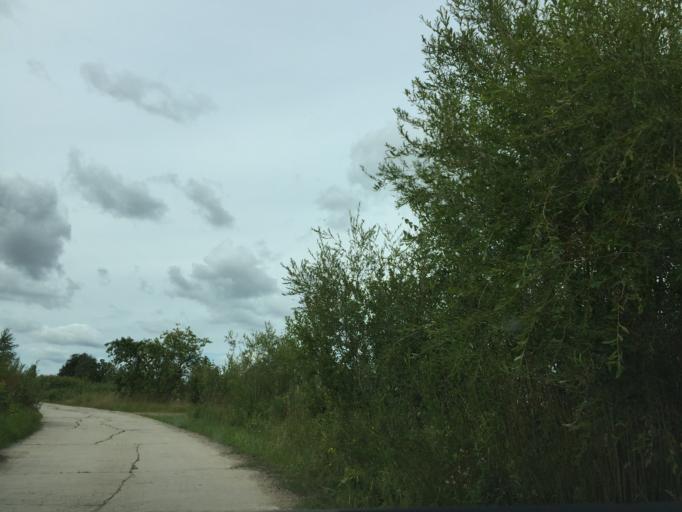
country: LV
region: Lielvarde
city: Lielvarde
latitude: 56.7572
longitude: 24.8486
